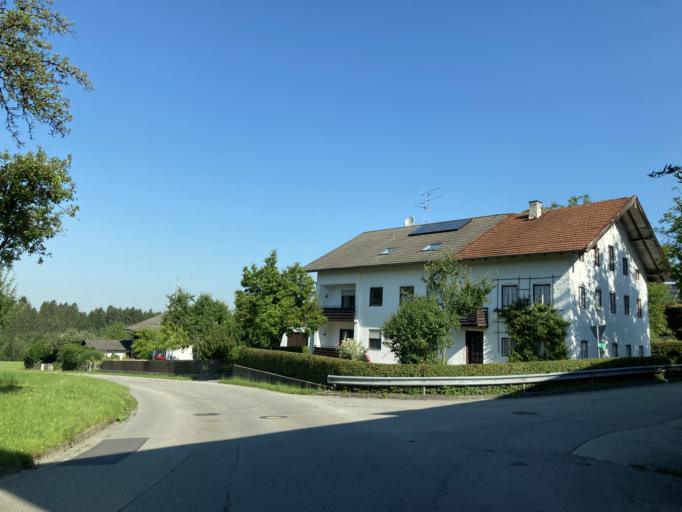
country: DE
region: Bavaria
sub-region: Upper Bavaria
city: Bad Endorf
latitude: 47.9112
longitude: 12.2817
